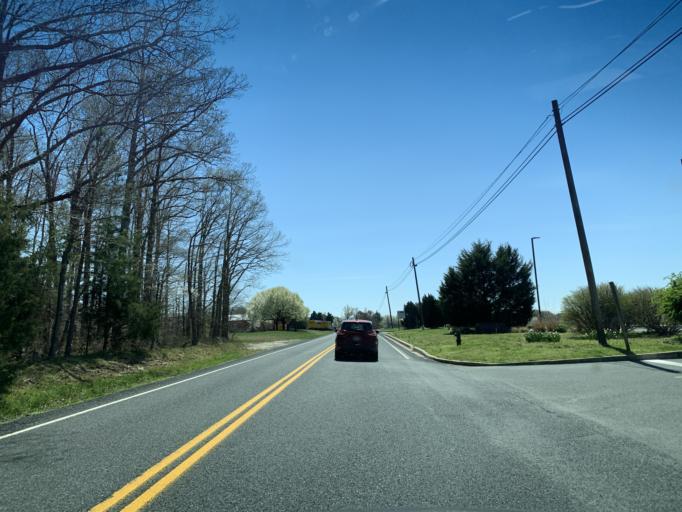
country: US
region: Maryland
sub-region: Talbot County
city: Easton
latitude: 38.8003
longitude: -76.0634
